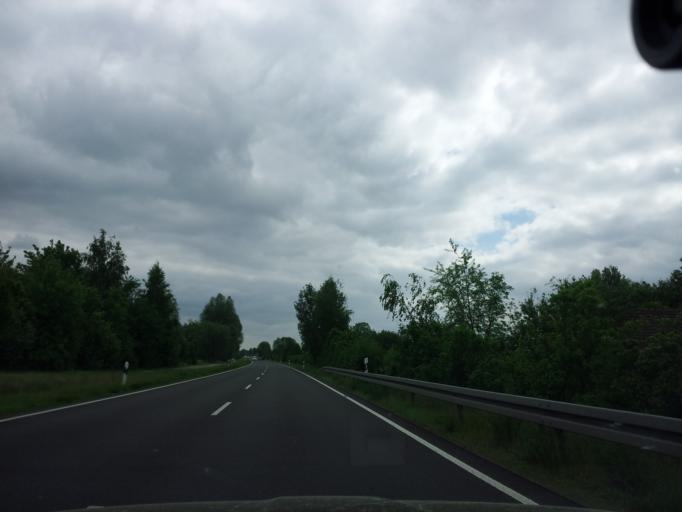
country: DE
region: Brandenburg
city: Beelitz
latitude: 52.2445
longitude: 12.9855
